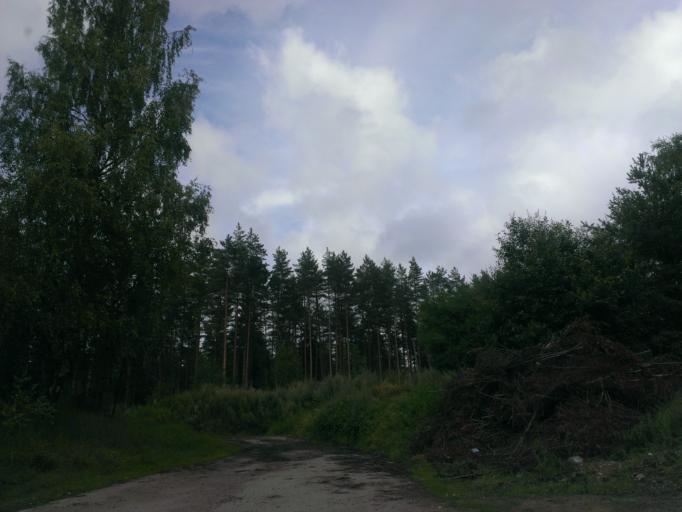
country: LV
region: Amatas Novads
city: Drabesi
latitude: 57.2210
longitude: 25.2166
